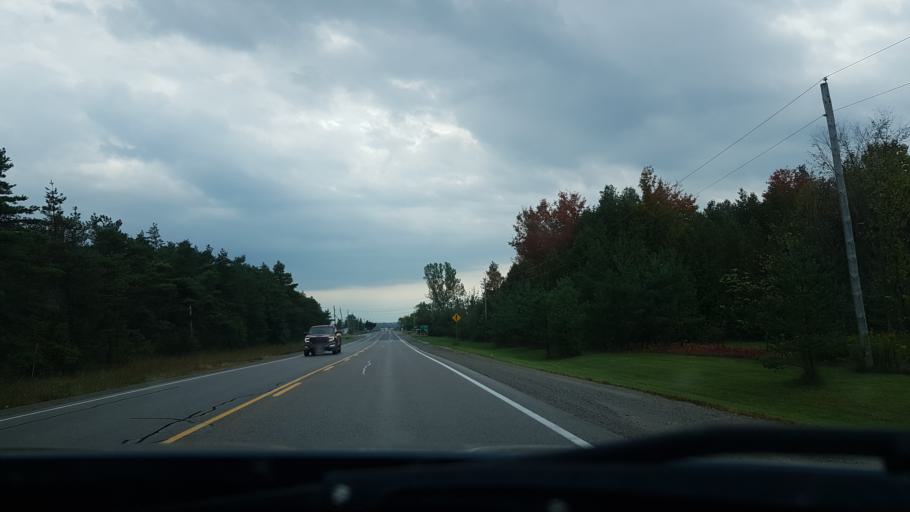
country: CA
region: Ontario
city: Omemee
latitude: 44.4290
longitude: -78.7788
